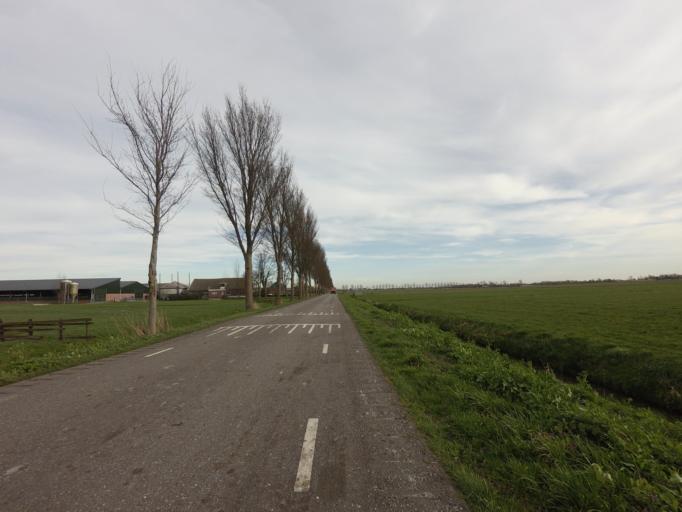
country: NL
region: Utrecht
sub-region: Gemeente De Ronde Venen
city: Mijdrecht
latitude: 52.1987
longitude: 4.8341
